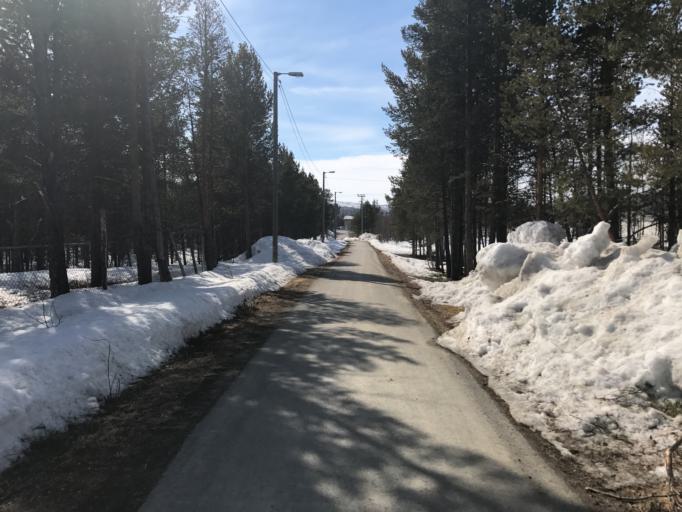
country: NO
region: Finnmark Fylke
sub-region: Karasjok
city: Karasjohka
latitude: 69.4766
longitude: 25.5184
